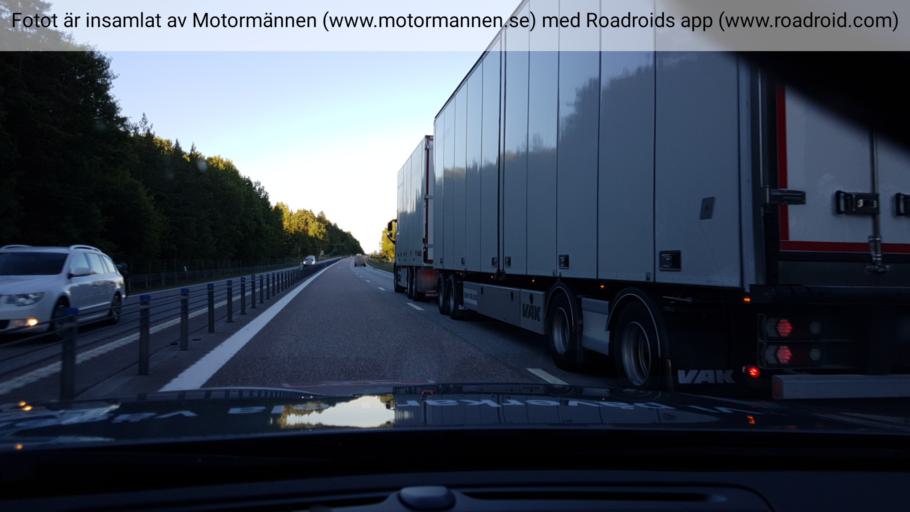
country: SE
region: Vaestmanland
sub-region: Hallstahammars Kommun
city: Hallstahammar
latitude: 59.5828
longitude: 16.1609
